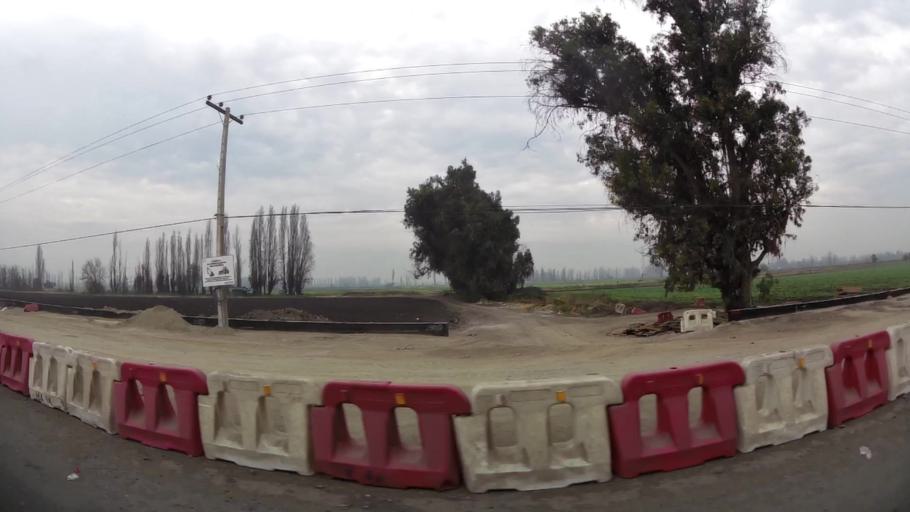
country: CL
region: Santiago Metropolitan
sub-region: Provincia de Chacabuco
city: Chicureo Abajo
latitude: -33.2603
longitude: -70.7475
